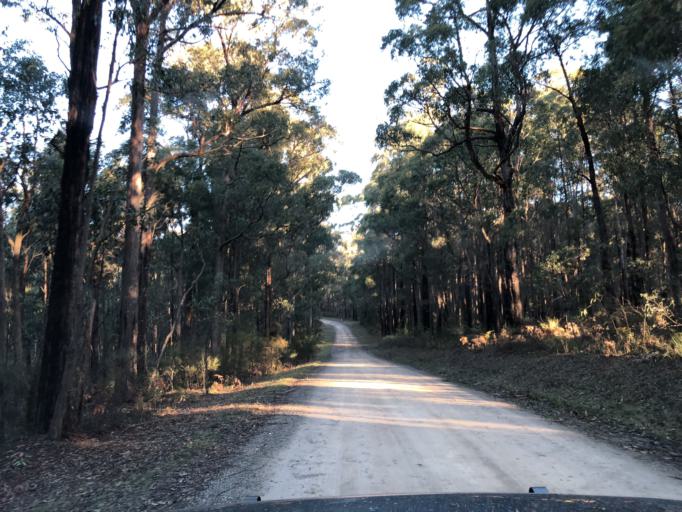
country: AU
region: Victoria
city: Brown Hill
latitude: -37.4778
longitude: 144.1835
